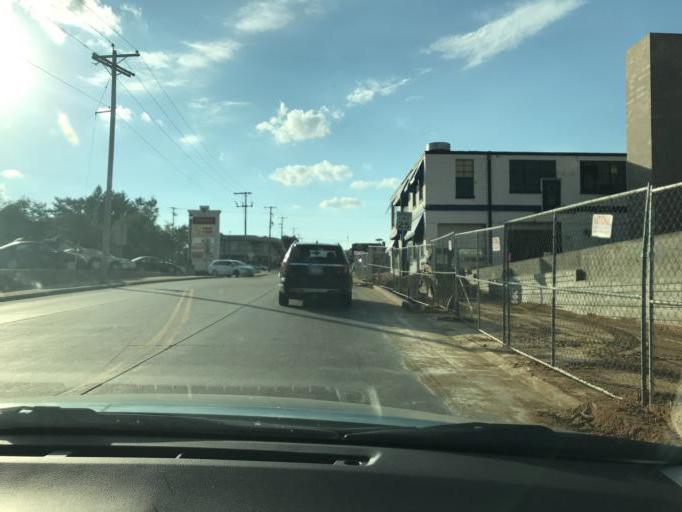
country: US
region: Wisconsin
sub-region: Grant County
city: Platteville
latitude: 42.7325
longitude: -90.4759
